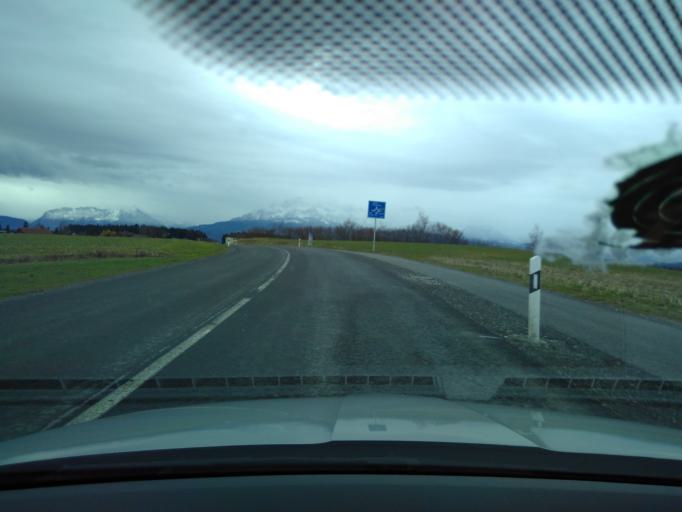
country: CH
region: Lucerne
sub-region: Sursee District
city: Hildisrieden
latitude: 47.1306
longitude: 8.2419
